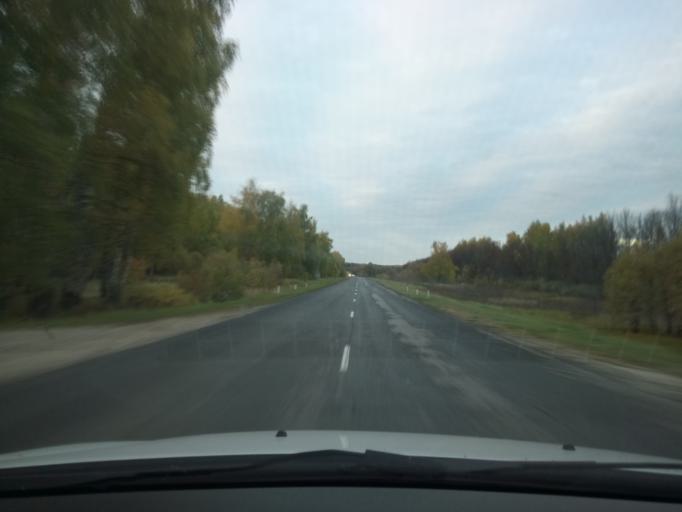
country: RU
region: Nizjnij Novgorod
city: Bol'shoye Murashkino
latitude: 55.7346
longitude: 44.7761
